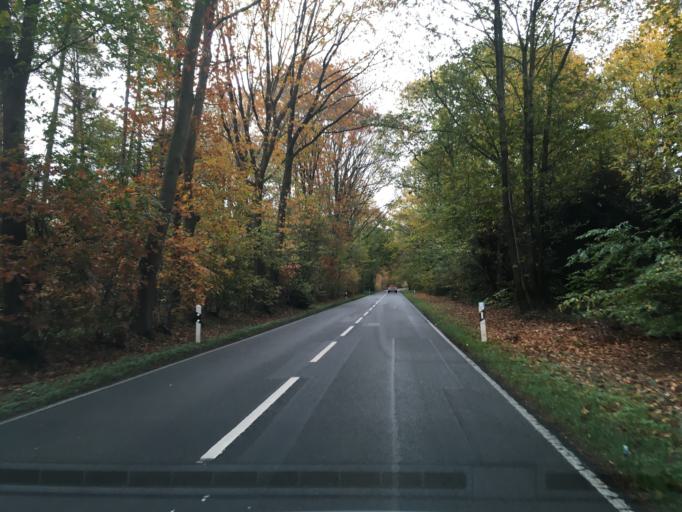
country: DE
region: North Rhine-Westphalia
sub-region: Regierungsbezirk Munster
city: Heiden
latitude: 51.8235
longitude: 6.9790
